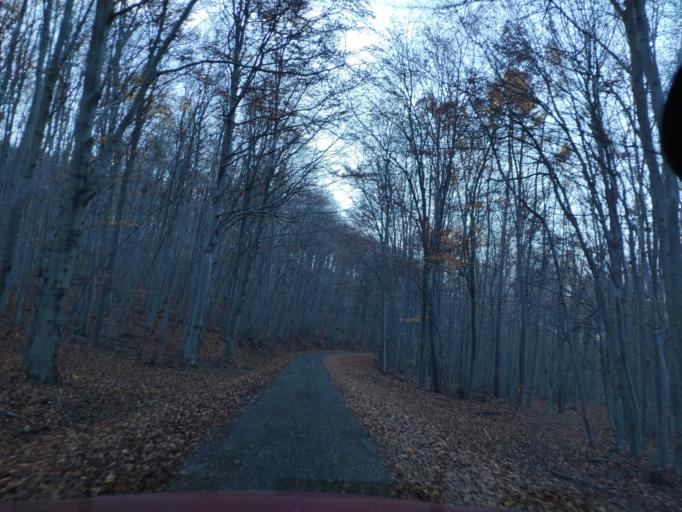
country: SK
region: Kosicky
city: Secovce
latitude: 48.5823
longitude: 21.5081
